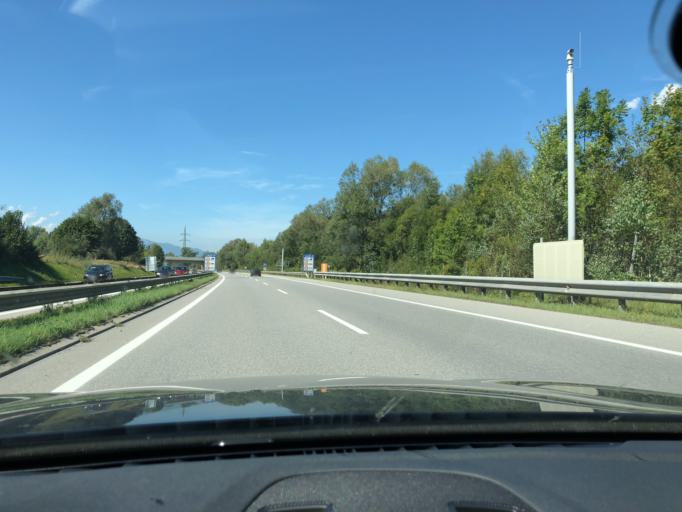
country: AT
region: Vorarlberg
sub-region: Politischer Bezirk Bludenz
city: Nuziders
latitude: 47.1694
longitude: 9.7850
